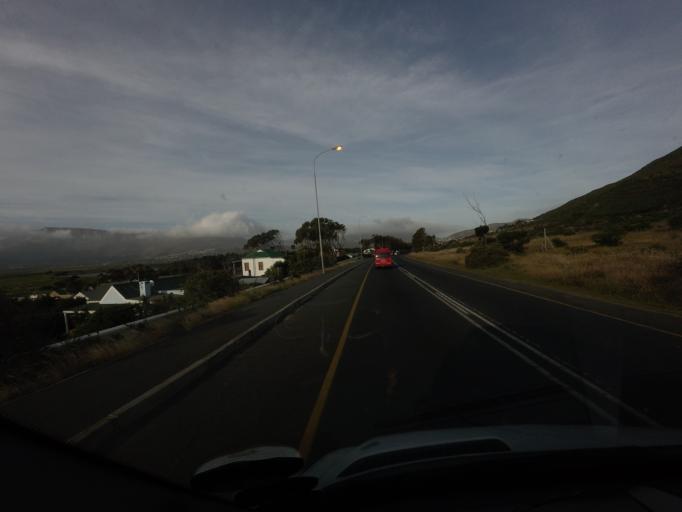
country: ZA
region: Western Cape
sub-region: City of Cape Town
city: Constantia
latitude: -34.1372
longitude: 18.3630
